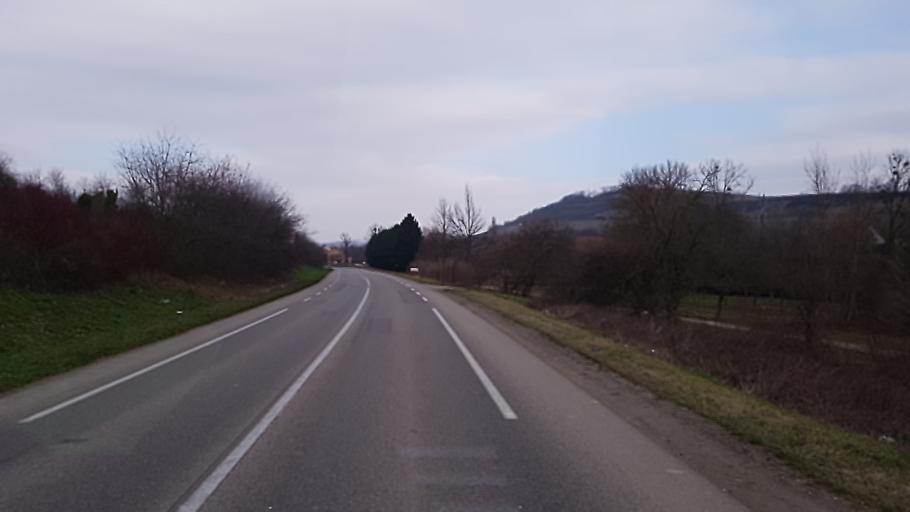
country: FR
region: Alsace
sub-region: Departement du Bas-Rhin
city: Molsheim
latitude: 48.5647
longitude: 7.4960
